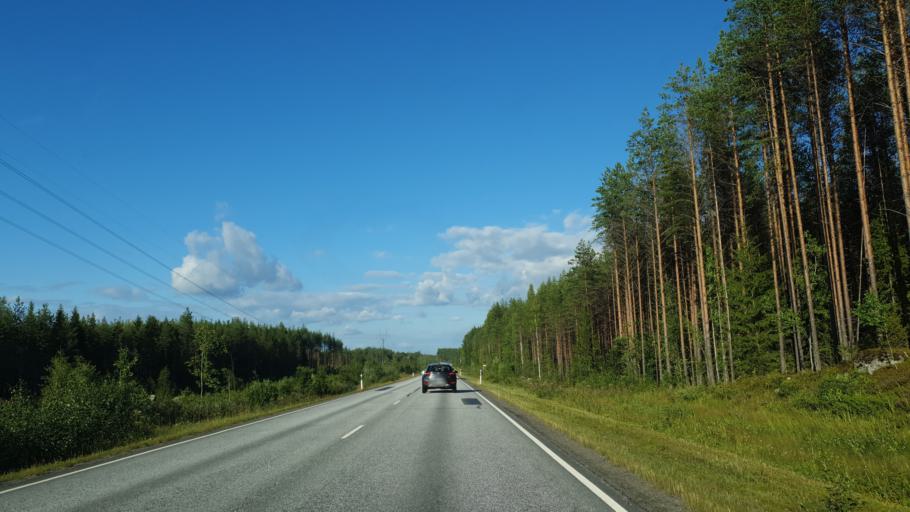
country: FI
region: North Karelia
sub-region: Joensuu
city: Outokumpu
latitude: 62.5307
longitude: 29.0864
